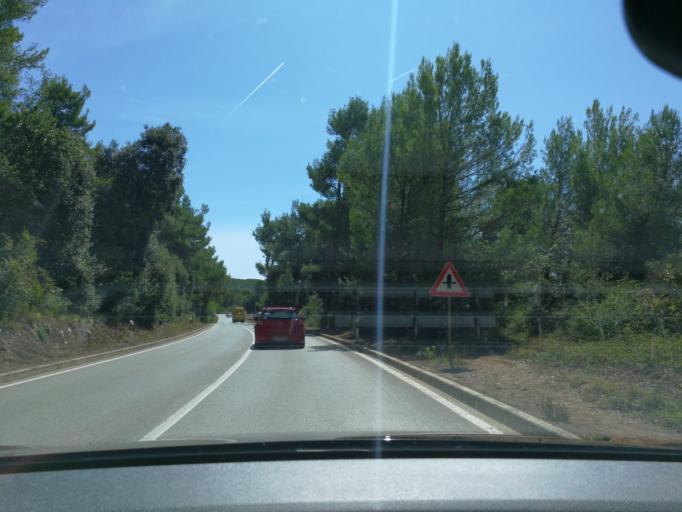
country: HR
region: Istarska
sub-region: Grad Pula
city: Pula
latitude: 44.8231
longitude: 13.8793
